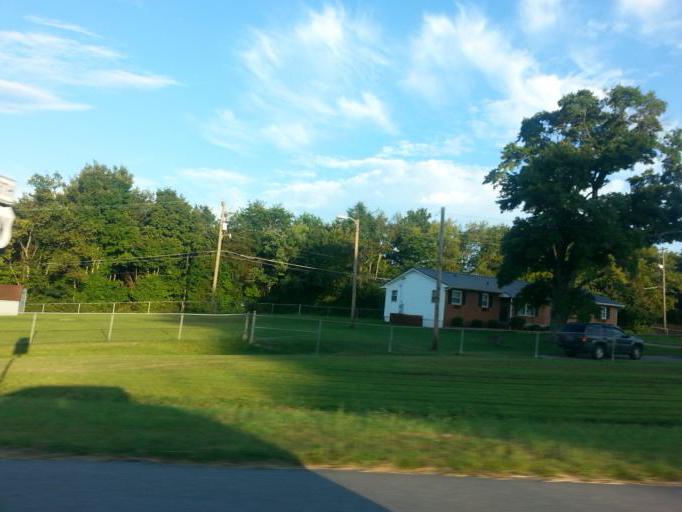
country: US
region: Tennessee
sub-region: Knox County
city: Mascot
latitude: 36.0696
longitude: -83.7748
